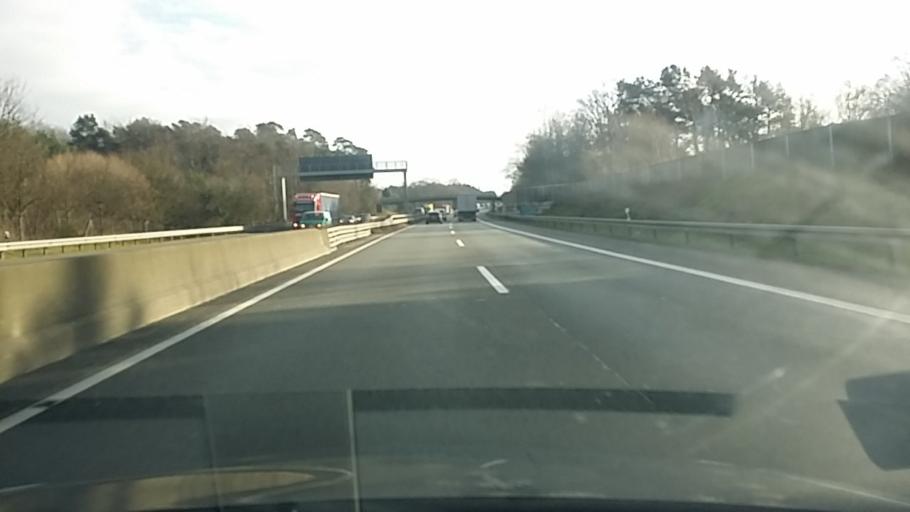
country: DE
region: North Rhine-Westphalia
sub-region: Regierungsbezirk Detmold
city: Verl
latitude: 51.9372
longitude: 8.5665
